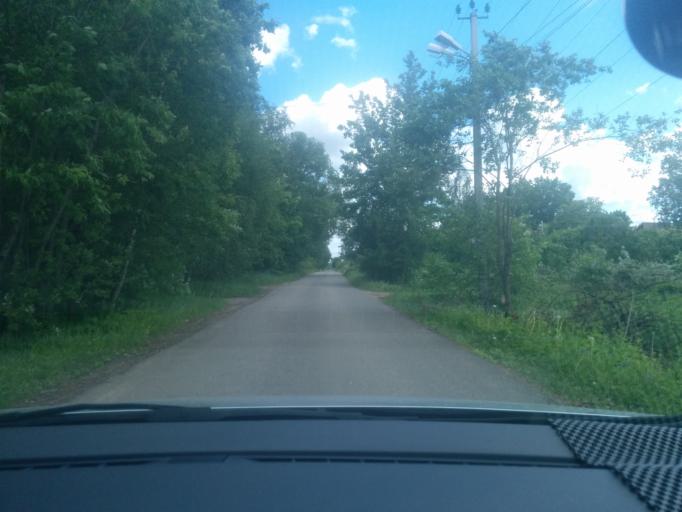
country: RU
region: Moskovskaya
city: Lugovaya
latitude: 56.0499
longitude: 37.5012
